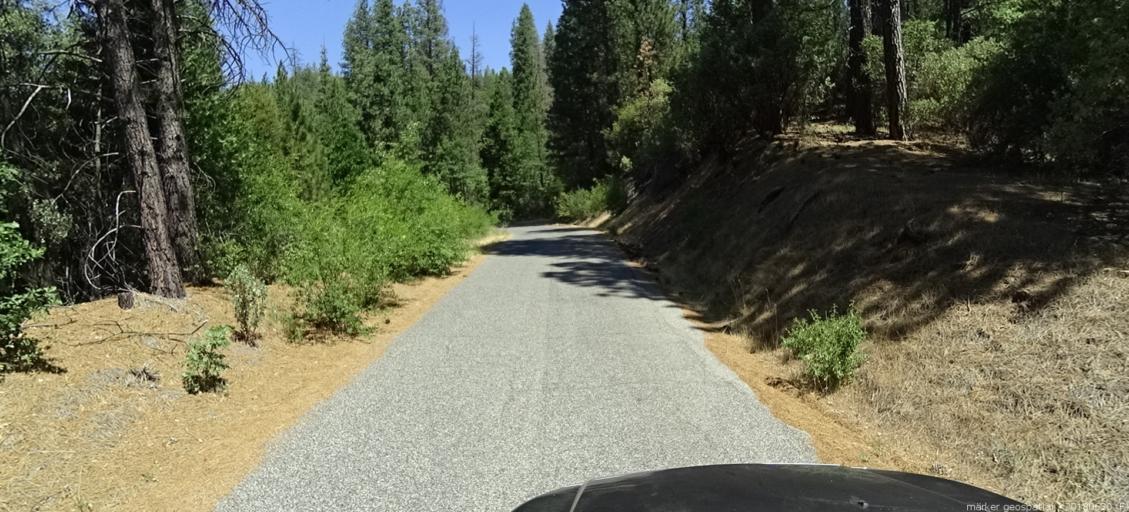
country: US
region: California
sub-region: Madera County
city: Oakhurst
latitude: 37.3588
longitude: -119.3446
